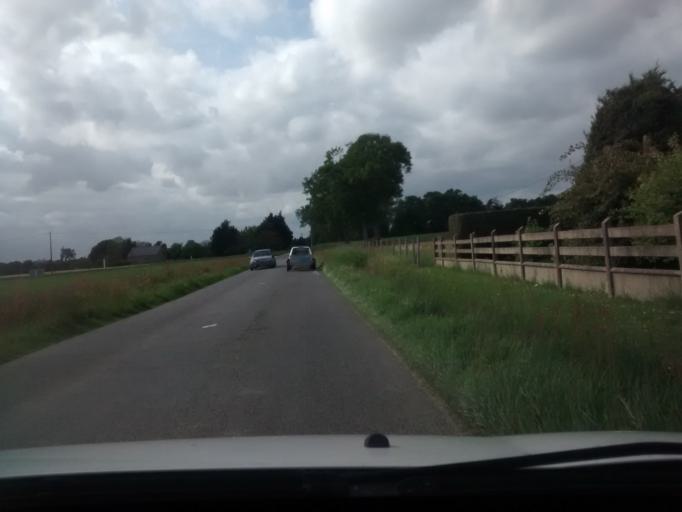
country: FR
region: Brittany
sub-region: Departement d'Ille-et-Vilaine
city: Nouvoitou
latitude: 48.0705
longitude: -1.5402
